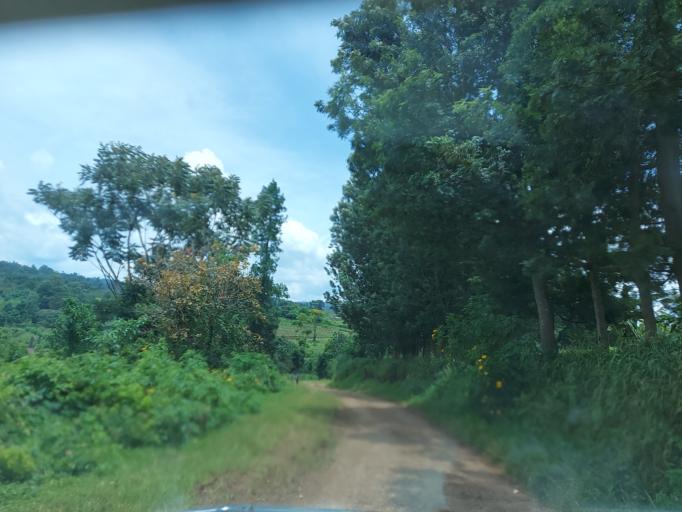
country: CD
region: South Kivu
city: Kabare
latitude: -2.3373
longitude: 28.7853
